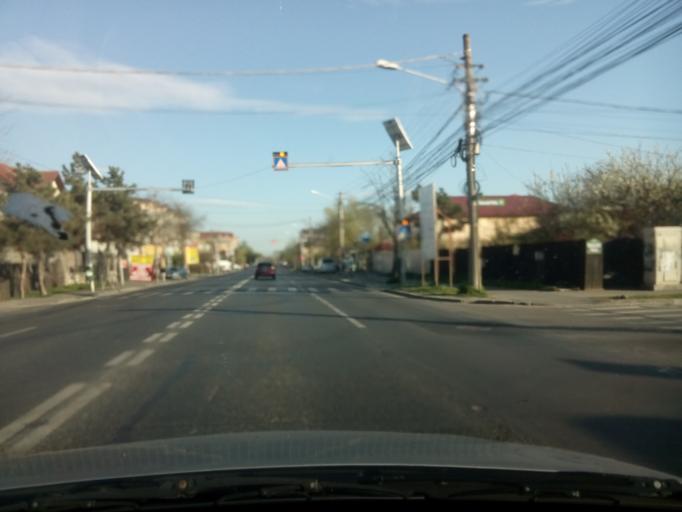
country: RO
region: Ilfov
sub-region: Comuna Mogosoaia
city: Mogosoaia
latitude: 44.5127
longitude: 26.0185
